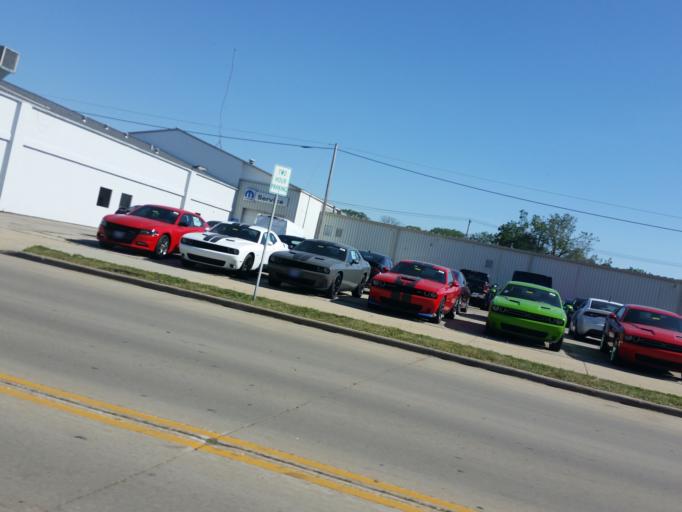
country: US
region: Illinois
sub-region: Winnebago County
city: South Beloit
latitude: 42.4987
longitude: -89.0321
